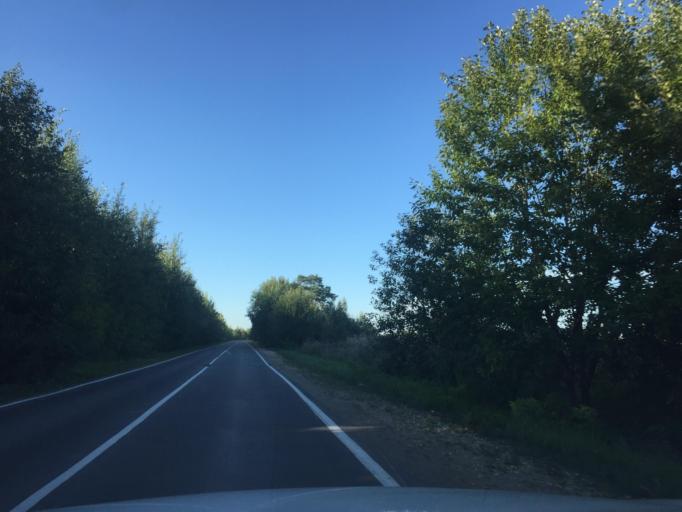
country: RU
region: Leningrad
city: Siverskiy
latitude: 59.3135
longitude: 30.0330
